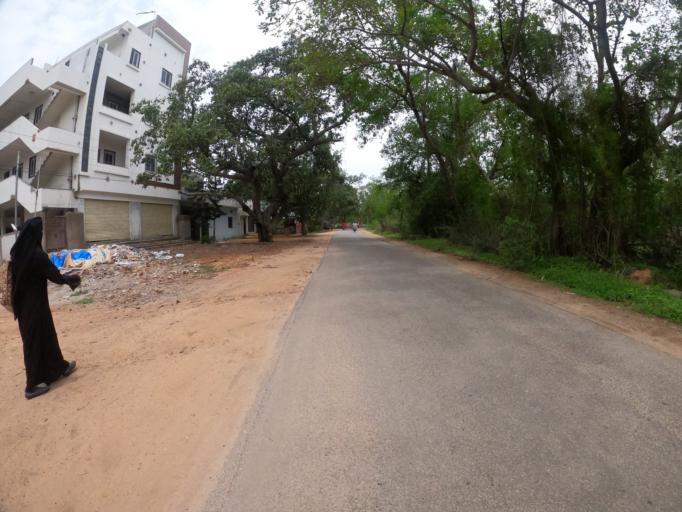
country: IN
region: Telangana
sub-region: Hyderabad
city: Hyderabad
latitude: 17.3472
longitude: 78.3760
